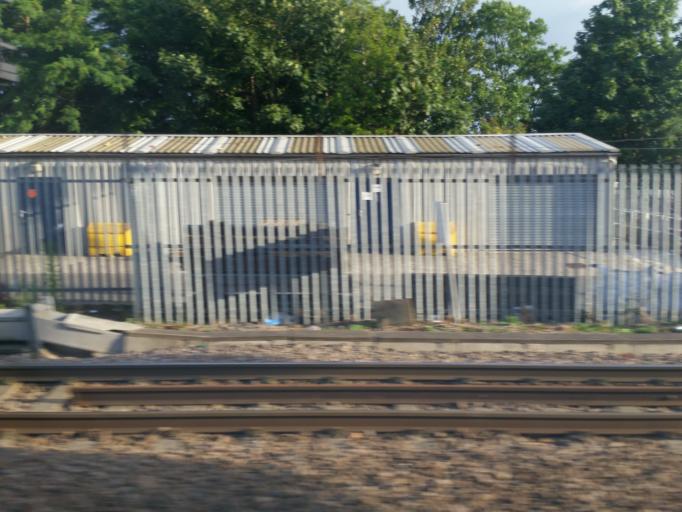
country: GB
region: England
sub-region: Greater London
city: Camden Town
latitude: 51.5413
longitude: -0.1342
